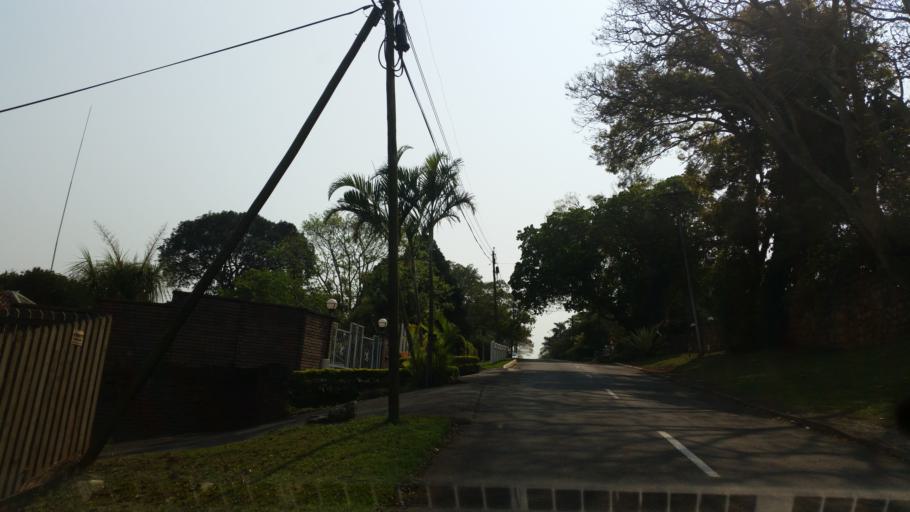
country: ZA
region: KwaZulu-Natal
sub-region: eThekwini Metropolitan Municipality
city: Berea
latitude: -29.7989
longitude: 30.8341
